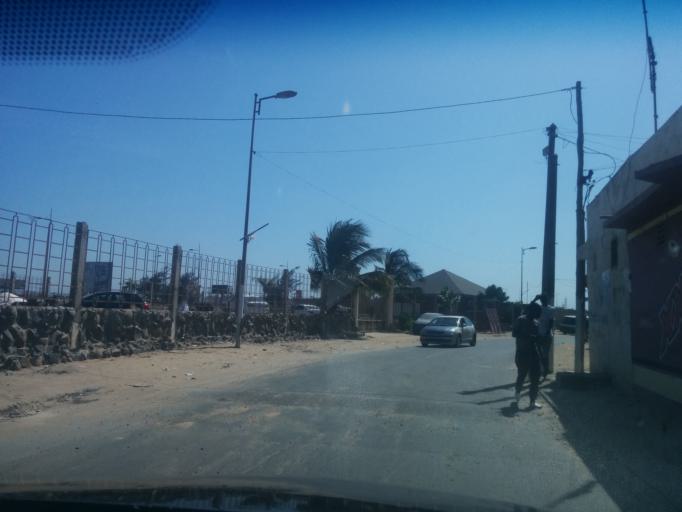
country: SN
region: Dakar
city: Grand Dakar
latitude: 14.7420
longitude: -17.4412
